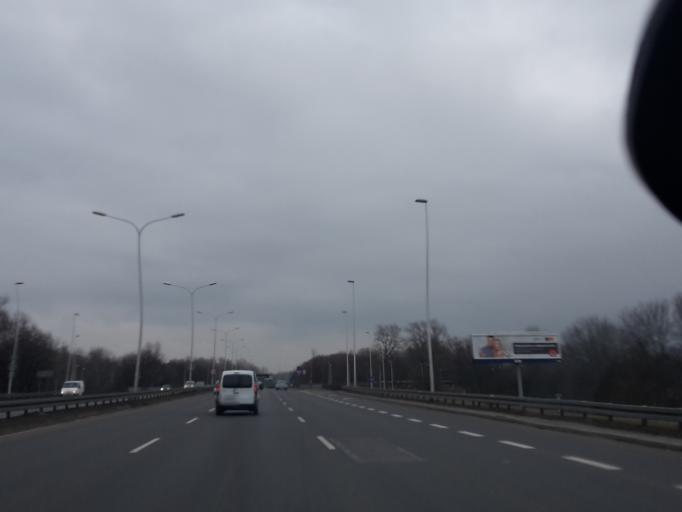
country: PL
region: Masovian Voivodeship
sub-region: Warszawa
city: Zoliborz
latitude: 52.2923
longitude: 20.9725
